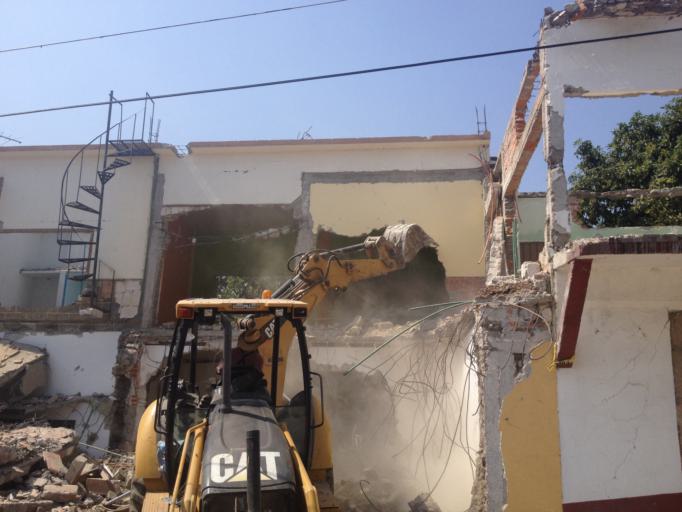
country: MX
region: Morelos
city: Jantetelco
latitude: 18.7147
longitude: -98.7759
